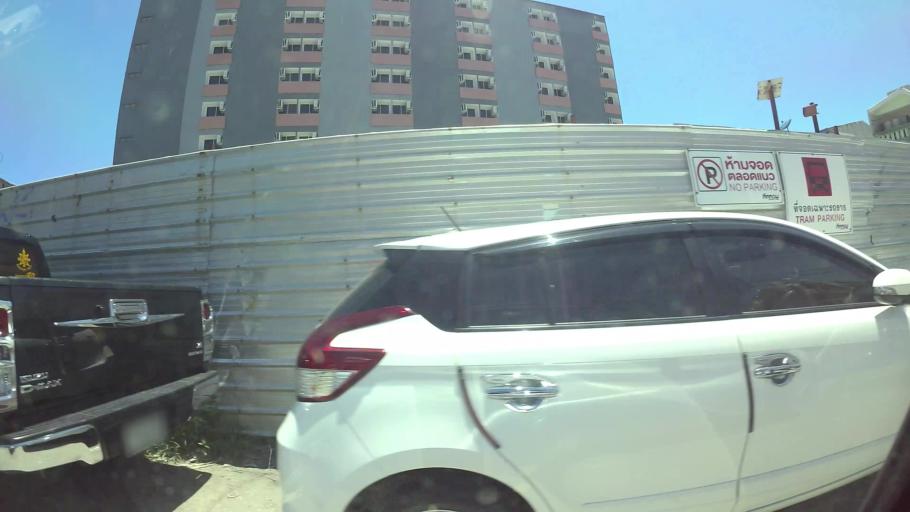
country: TH
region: Chon Buri
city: Phatthaya
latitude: 12.9225
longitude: 100.8794
